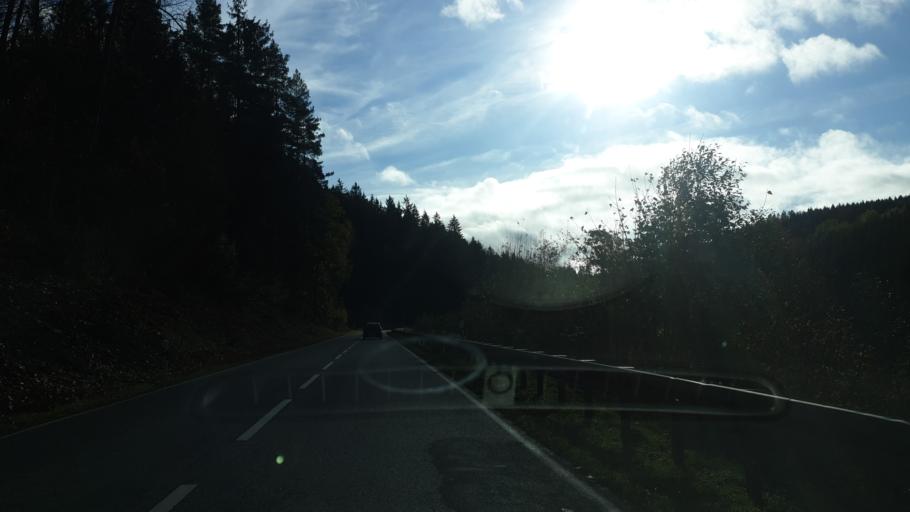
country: DE
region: Saxony
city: Bockau
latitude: 50.5663
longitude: 12.6926
